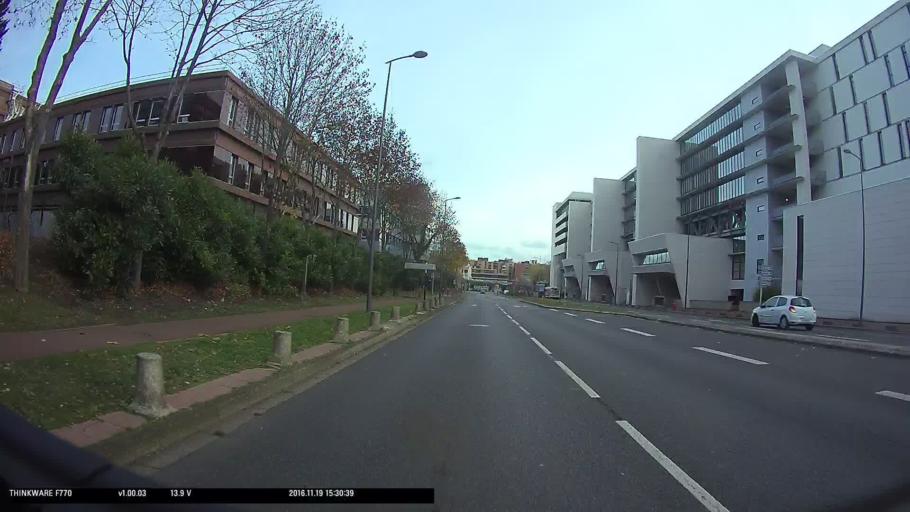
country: FR
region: Ile-de-France
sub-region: Departement du Val-d'Oise
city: Cergy-Pontoise
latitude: 49.0405
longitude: 2.0749
